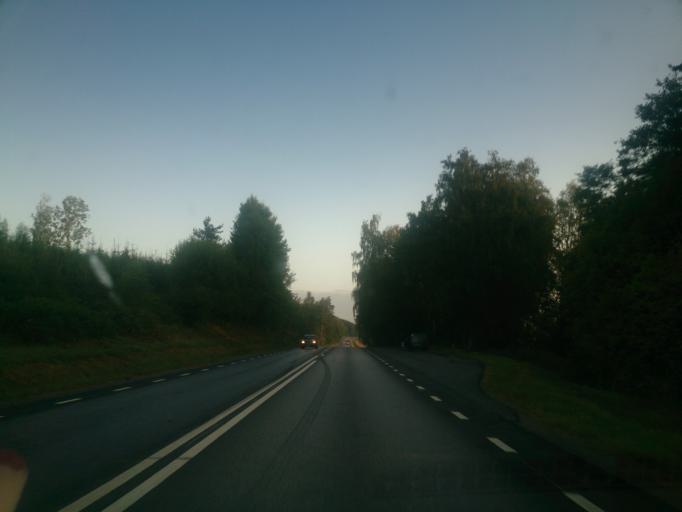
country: SE
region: Soedermanland
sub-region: Nykopings Kommun
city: Nykoping
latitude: 58.8018
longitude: 17.0826
